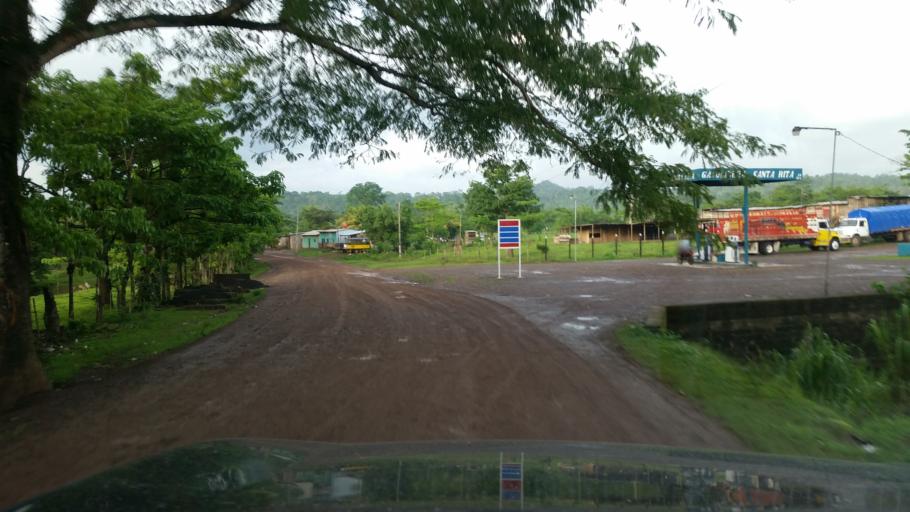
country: NI
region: Atlantico Norte (RAAN)
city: Siuna
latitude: 13.3694
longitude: -84.8698
